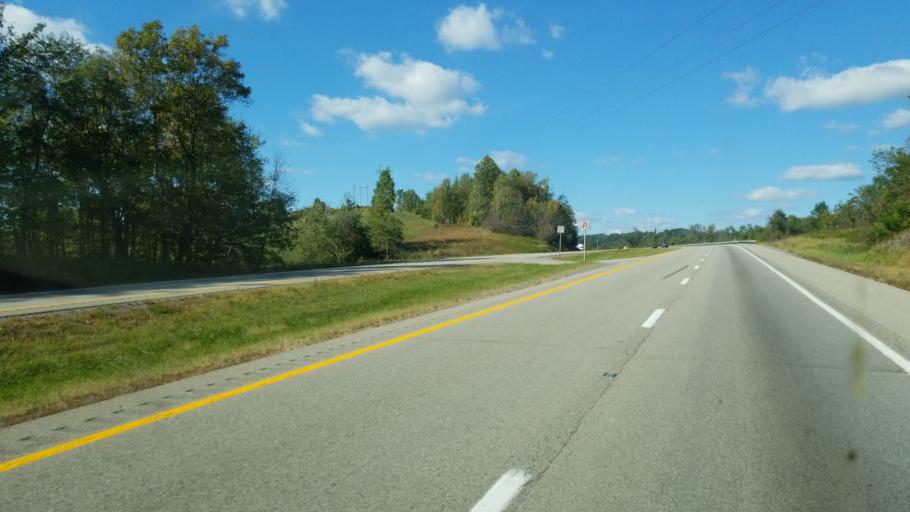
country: US
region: West Virginia
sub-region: Monongalia County
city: Star City
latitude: 39.6846
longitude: -80.0393
